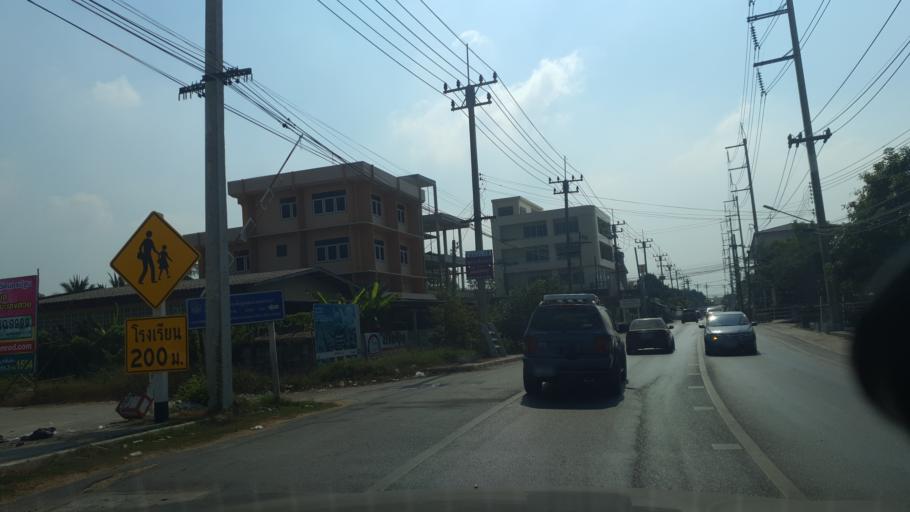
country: TH
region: Nakhon Pathom
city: Salaya
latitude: 13.7731
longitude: 100.2848
